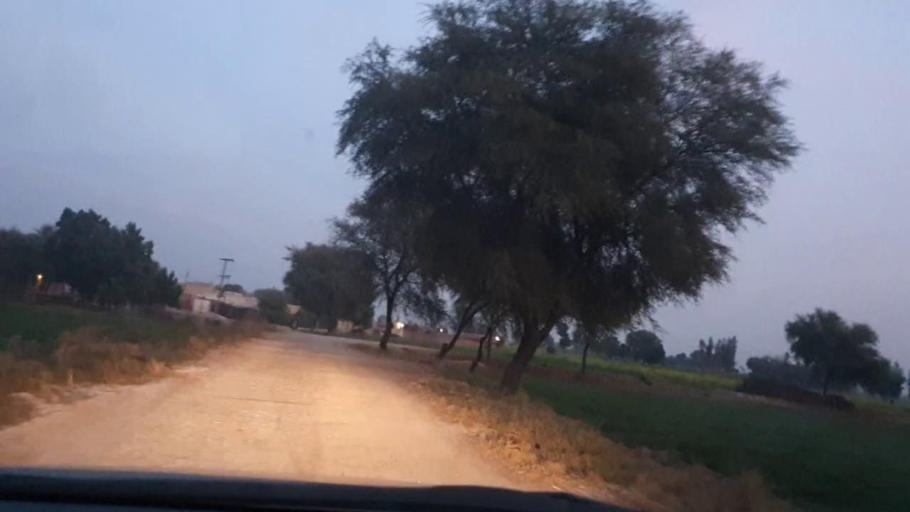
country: PK
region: Sindh
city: Sakrand
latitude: 26.1933
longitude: 68.3008
